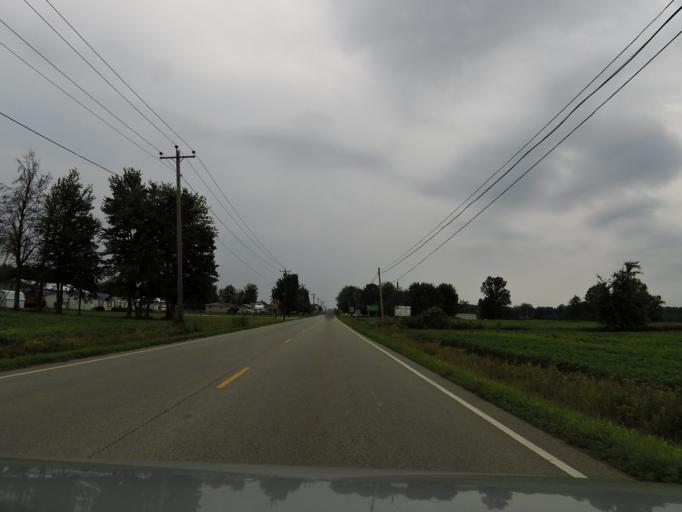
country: US
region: Ohio
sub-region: Brown County
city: Georgetown
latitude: 38.9177
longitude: -83.9032
